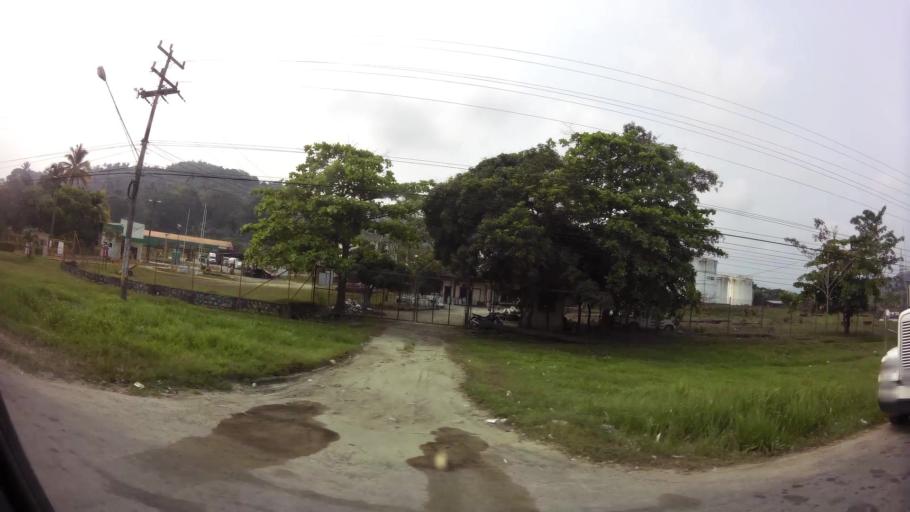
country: HN
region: Atlantida
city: El Triunfo de la Cruz
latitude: 15.7725
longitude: -87.4498
